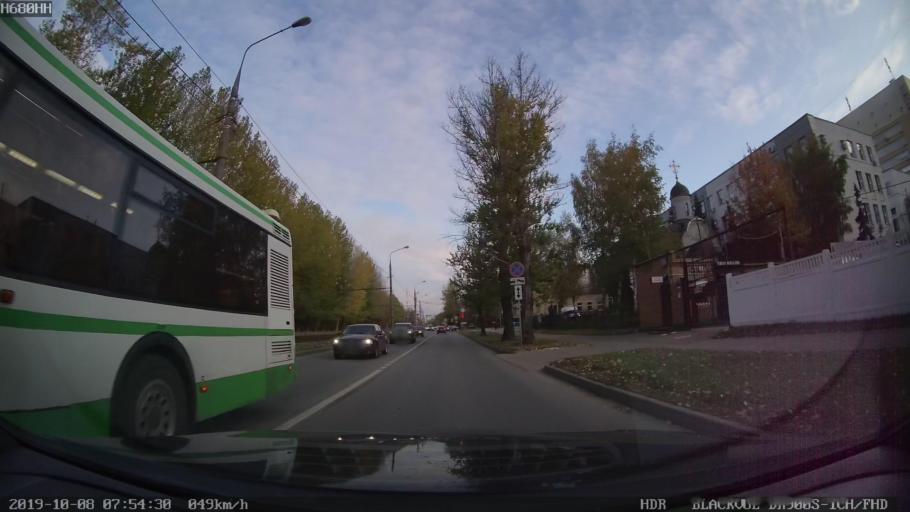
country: RU
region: Moscow
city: Shchukino
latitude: 55.7908
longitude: 37.4544
